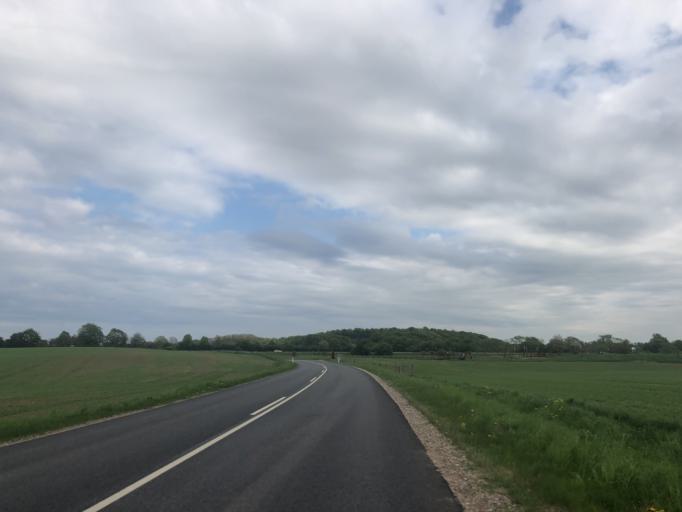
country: DK
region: Zealand
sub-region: Koge Kommune
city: Ejby
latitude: 55.4716
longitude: 12.1205
